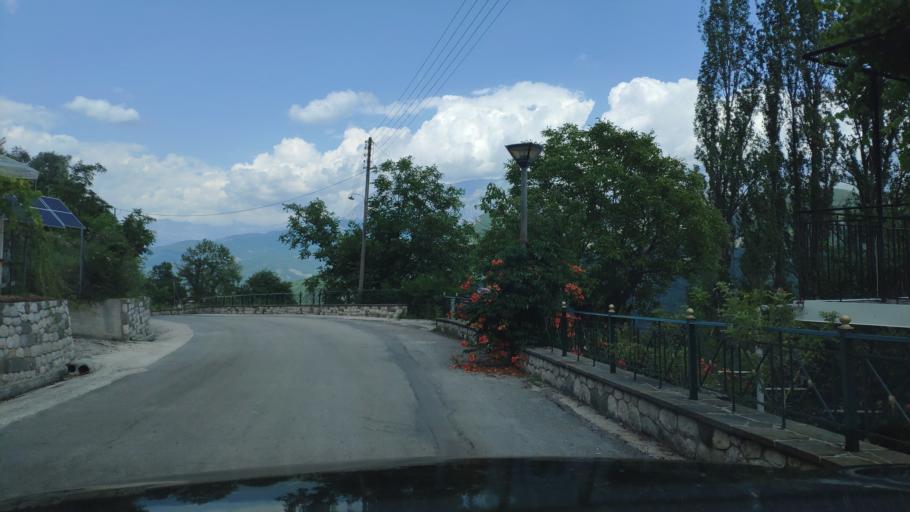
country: GR
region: Epirus
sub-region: Nomos Artas
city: Agios Dimitrios
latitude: 39.4179
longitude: 21.0107
